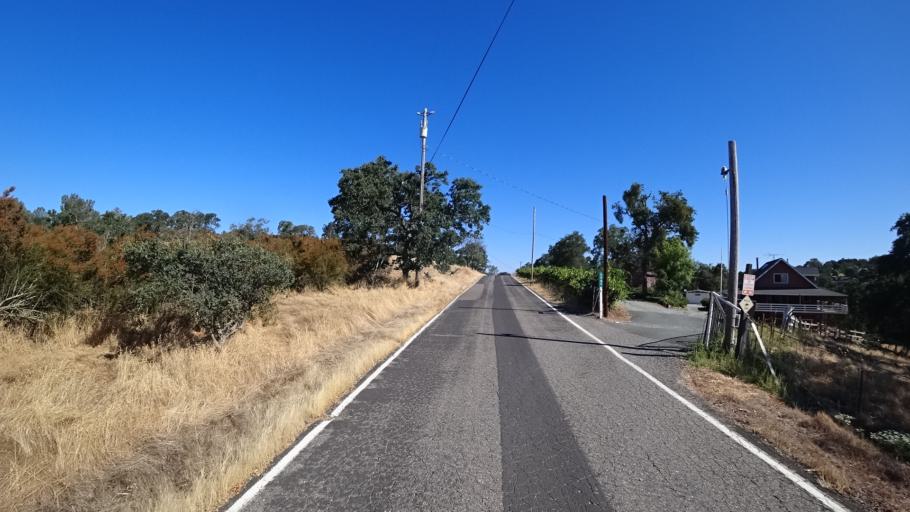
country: US
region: California
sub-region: Calaveras County
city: Rancho Calaveras
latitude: 38.1311
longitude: -120.8552
